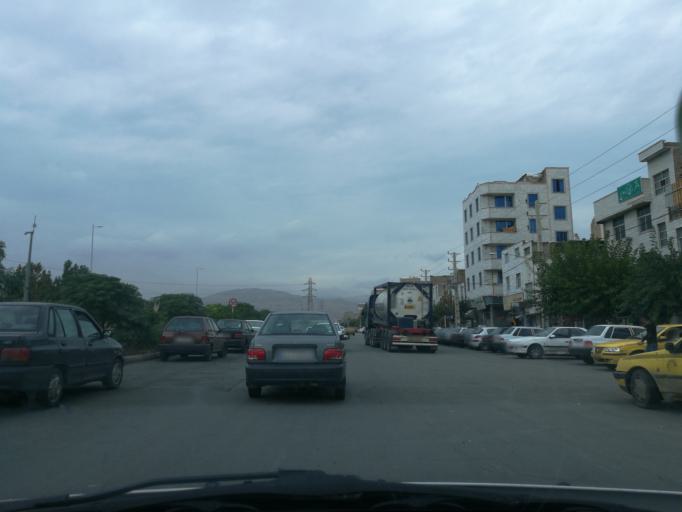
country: IR
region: Alborz
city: Karaj
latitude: 35.8479
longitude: 50.9159
